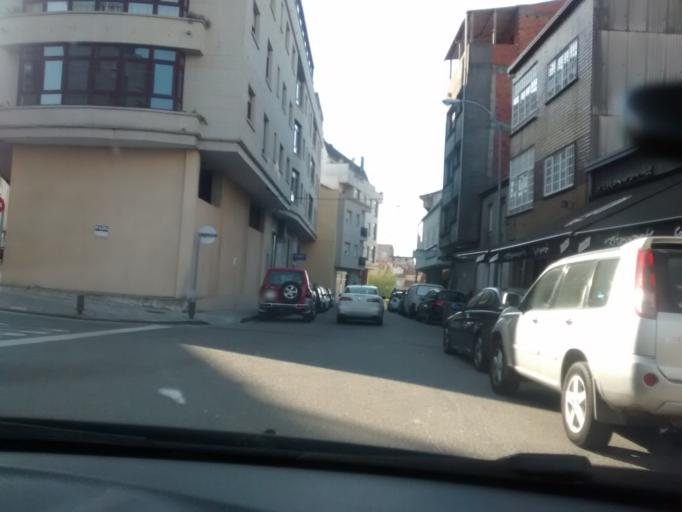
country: ES
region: Galicia
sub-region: Provincia de Pontevedra
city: A Estrada
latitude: 42.6906
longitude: -8.4875
